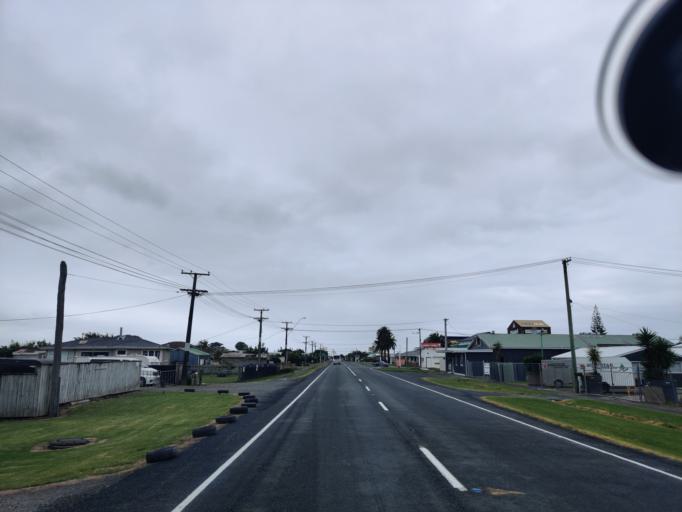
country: NZ
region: Northland
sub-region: Kaipara District
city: Dargaville
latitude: -36.1331
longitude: 174.0211
